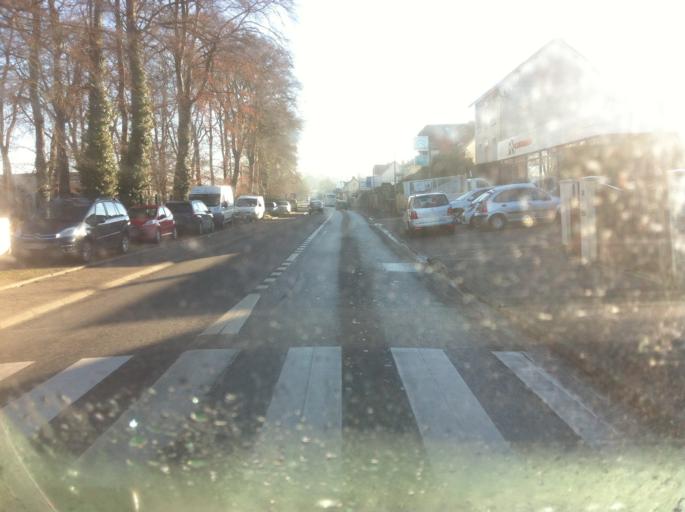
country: FR
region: Picardie
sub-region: Departement de la Somme
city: Mers-les-Bains
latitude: 50.0552
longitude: 1.3900
